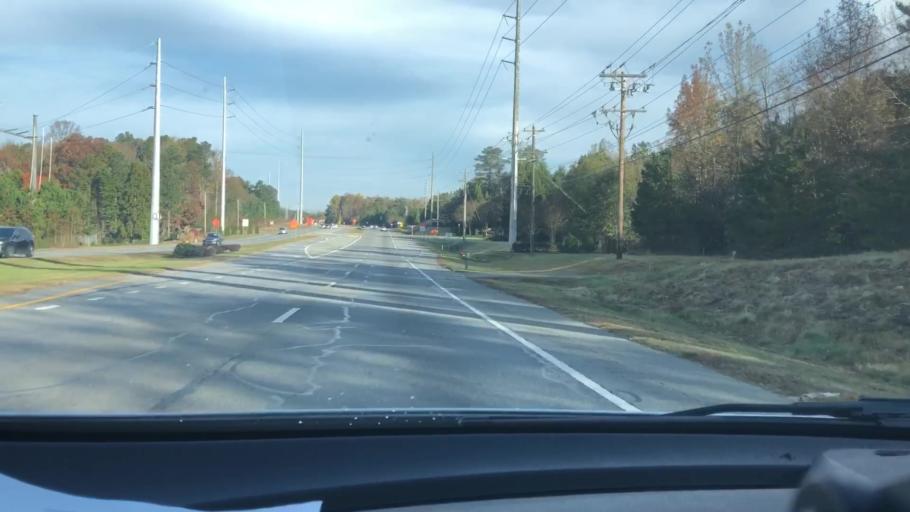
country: US
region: Georgia
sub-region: Forsyth County
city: Cumming
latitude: 34.1274
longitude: -84.1711
